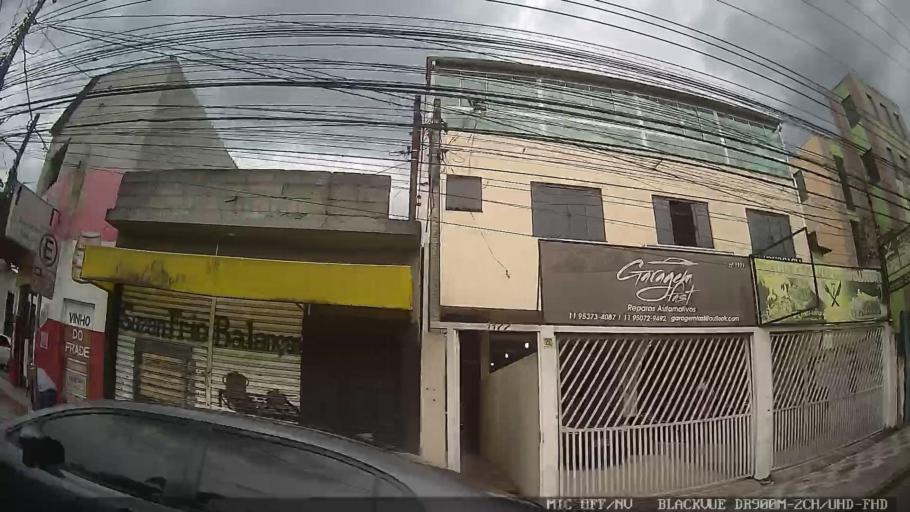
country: BR
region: Sao Paulo
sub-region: Suzano
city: Suzano
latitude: -23.5457
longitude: -46.3067
